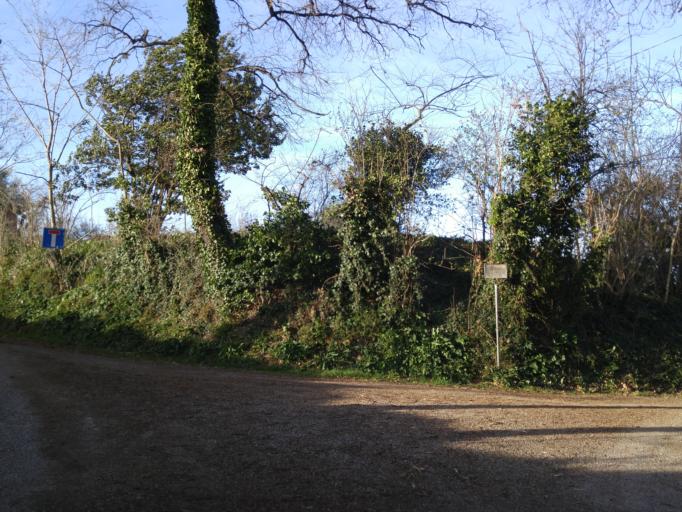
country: IT
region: The Marches
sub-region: Provincia di Pesaro e Urbino
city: Cartoceto
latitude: 43.7740
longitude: 12.8906
